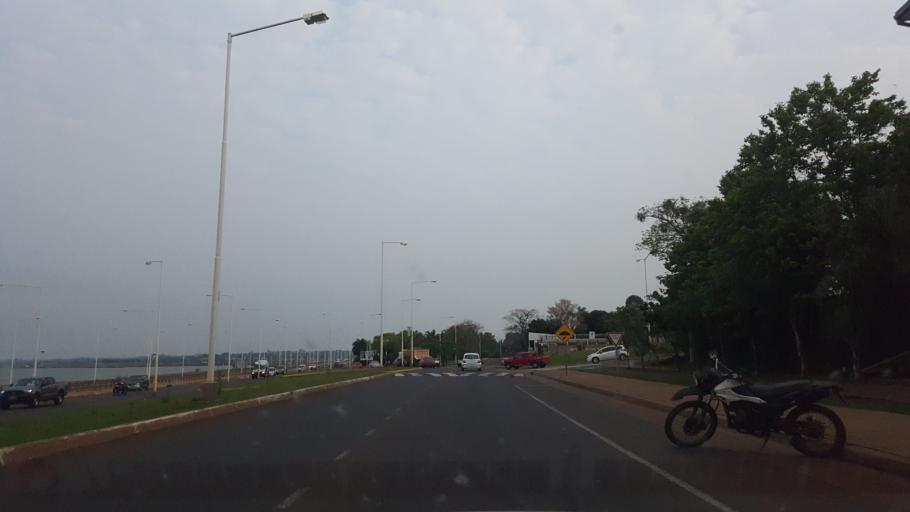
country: AR
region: Misiones
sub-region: Departamento de Capital
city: Posadas
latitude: -27.3981
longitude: -55.8928
